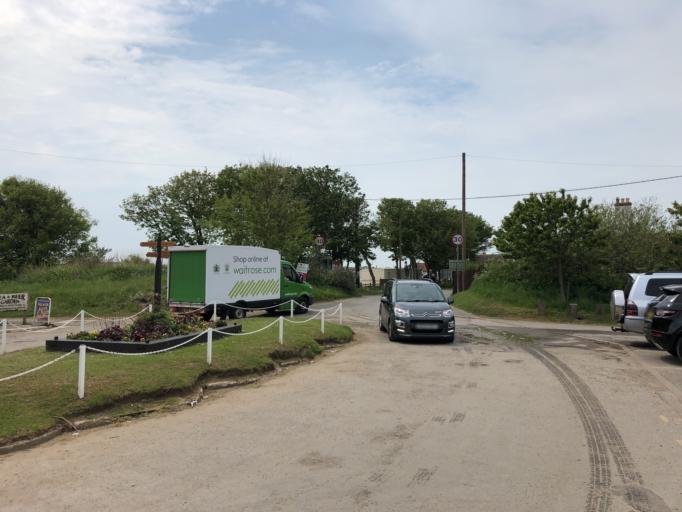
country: GB
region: England
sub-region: Lincolnshire
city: Chapel Saint Leonards
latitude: 53.2596
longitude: 0.3240
